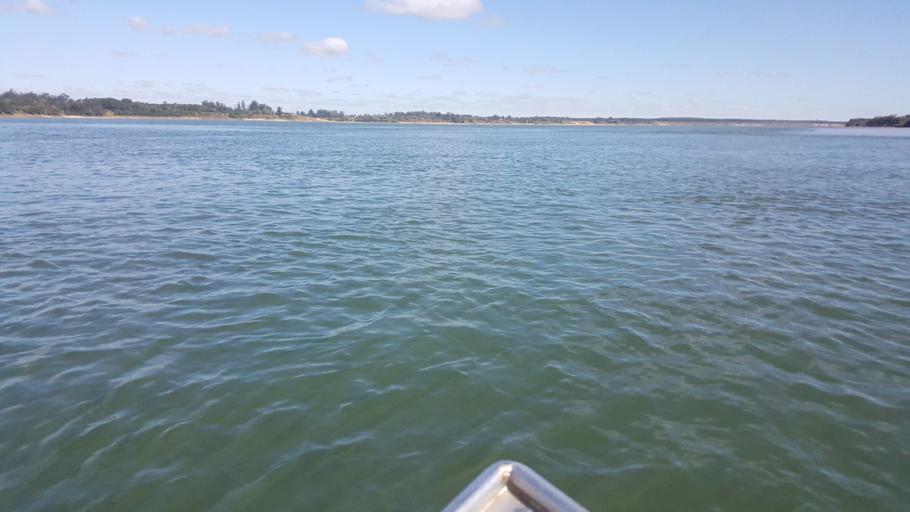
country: AR
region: Corrientes
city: Ituzaingo
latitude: -27.5817
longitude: -56.7116
